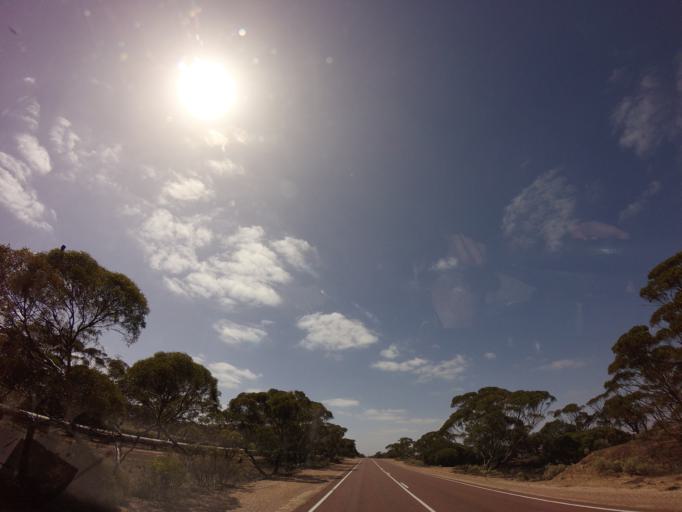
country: AU
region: South Australia
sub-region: Kimba
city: Caralue
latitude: -33.1093
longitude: 135.5296
